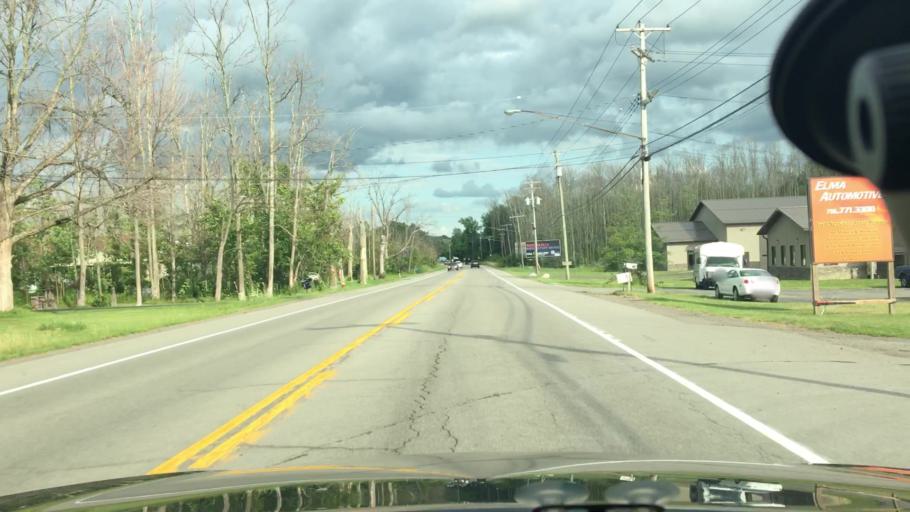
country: US
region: New York
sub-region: Erie County
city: Elma Center
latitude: 42.8249
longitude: -78.6880
